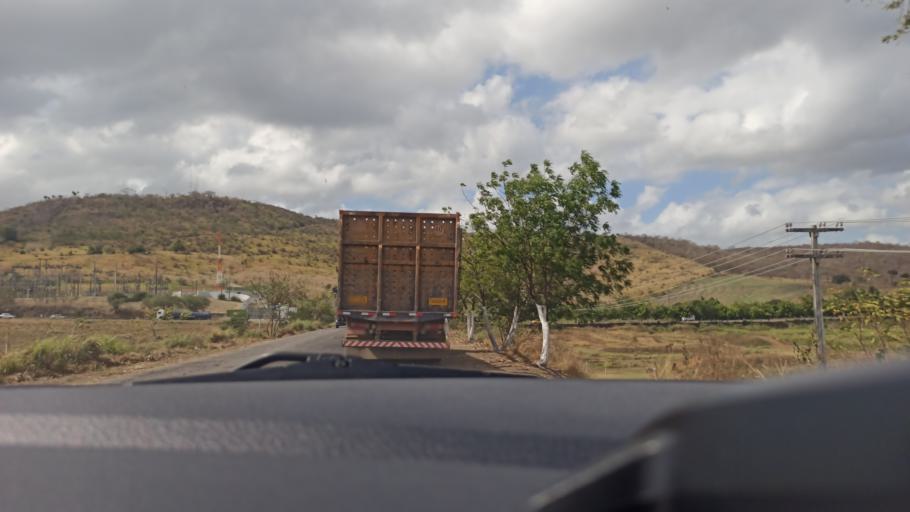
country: BR
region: Pernambuco
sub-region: Timbauba
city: Timbauba
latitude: -7.5191
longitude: -35.3050
